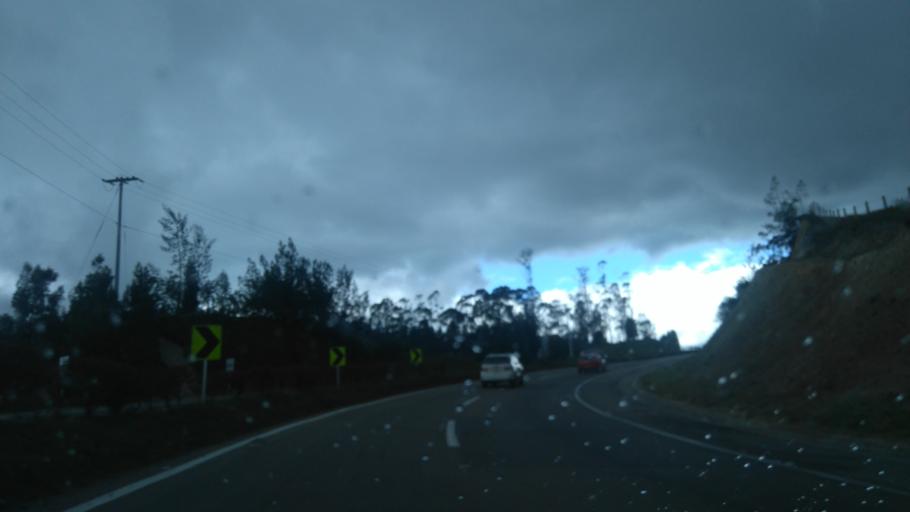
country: CO
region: Cundinamarca
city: El Rosal
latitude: 4.8751
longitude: -74.2952
